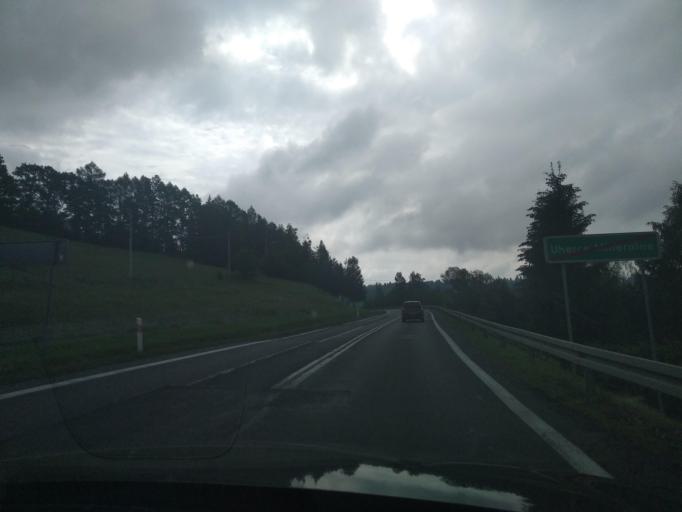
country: PL
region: Subcarpathian Voivodeship
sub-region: Powiat leski
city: Uherce Mineralne
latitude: 49.4713
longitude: 22.4181
